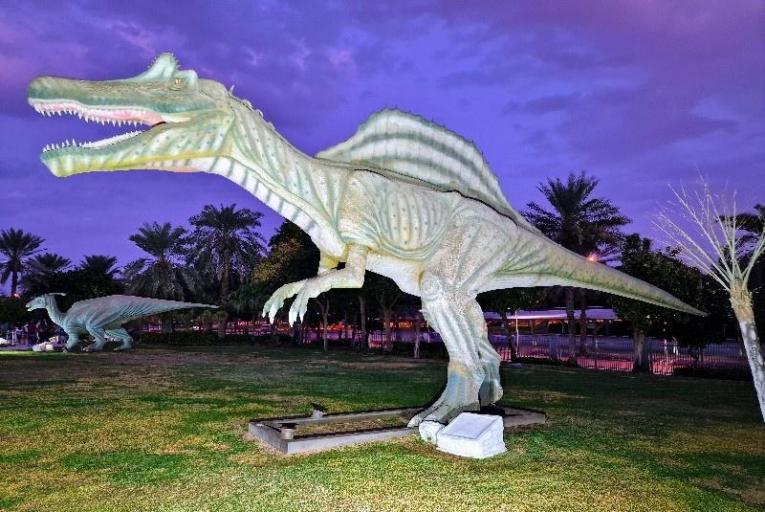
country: AE
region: Ash Shariqah
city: Sharjah
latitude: 25.2276
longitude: 55.2983
